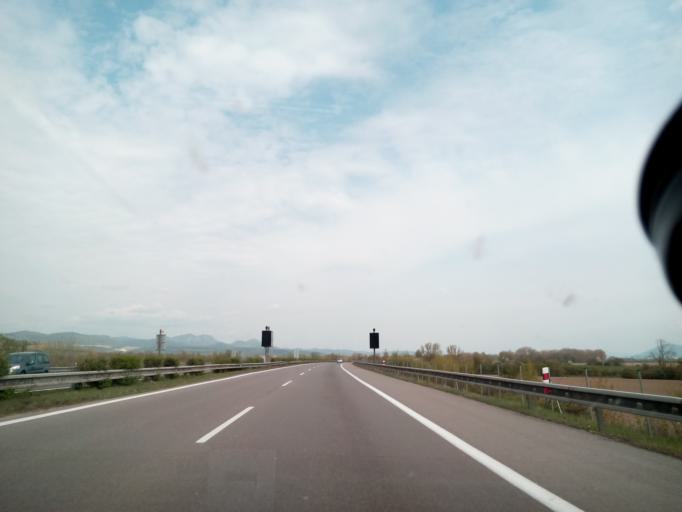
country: SK
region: Nitriansky
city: Nemsova
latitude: 48.9350
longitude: 18.0895
